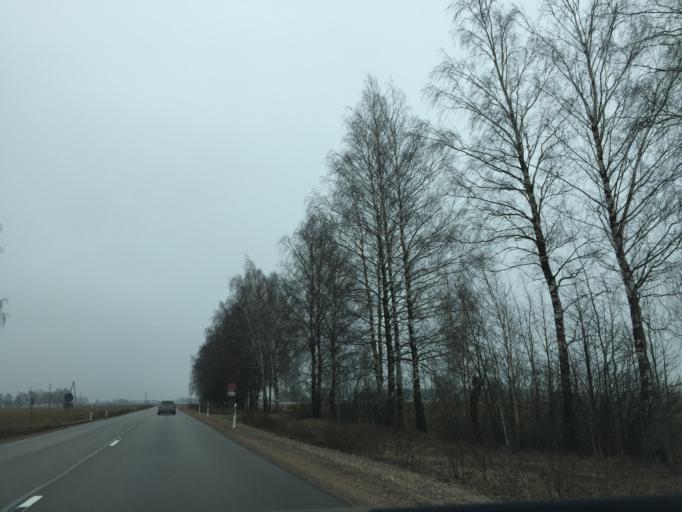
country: LV
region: Lecava
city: Iecava
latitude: 56.5997
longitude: 24.0981
